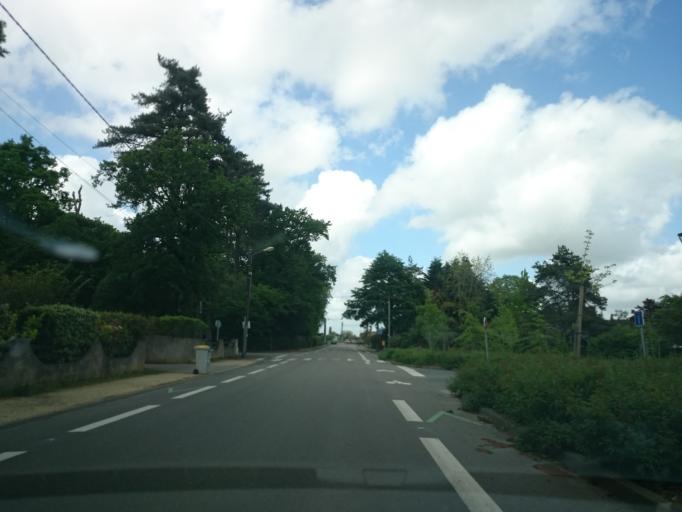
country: FR
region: Pays de la Loire
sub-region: Departement de la Loire-Atlantique
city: Bouaye
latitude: 47.1402
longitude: -1.6726
